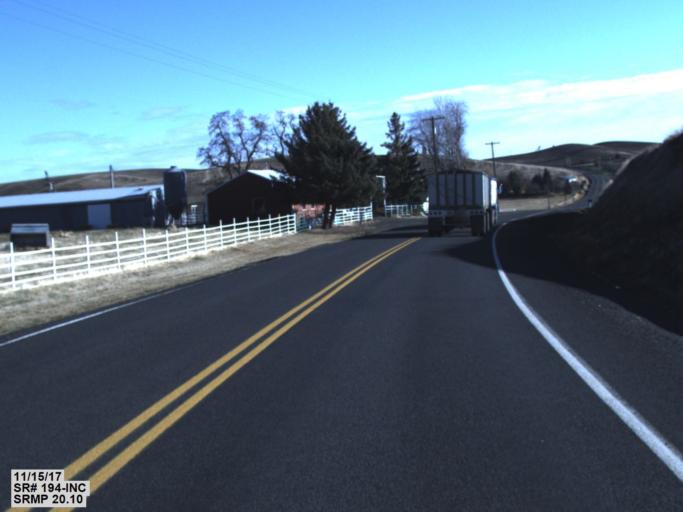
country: US
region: Washington
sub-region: Whitman County
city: Pullman
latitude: 46.7250
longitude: -117.2414
